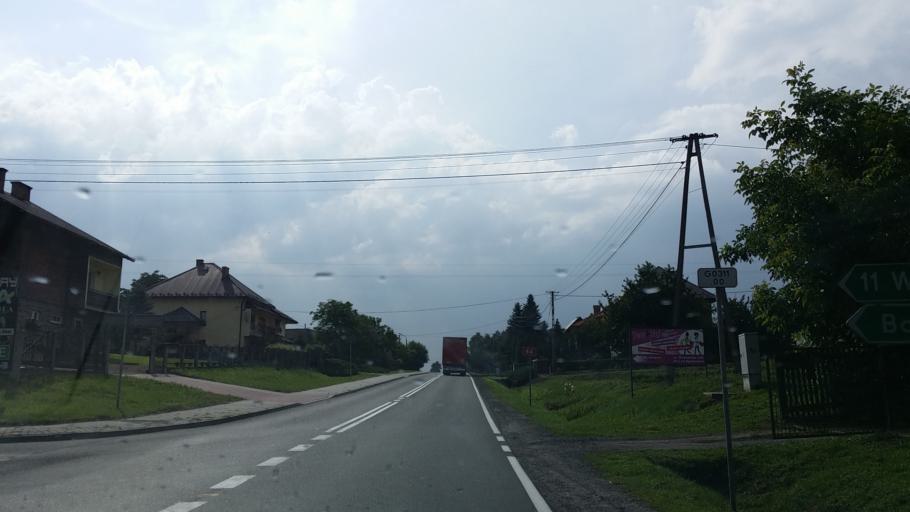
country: PL
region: Lesser Poland Voivodeship
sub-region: Powiat wadowicki
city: Spytkowice
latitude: 49.9933
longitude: 19.5029
